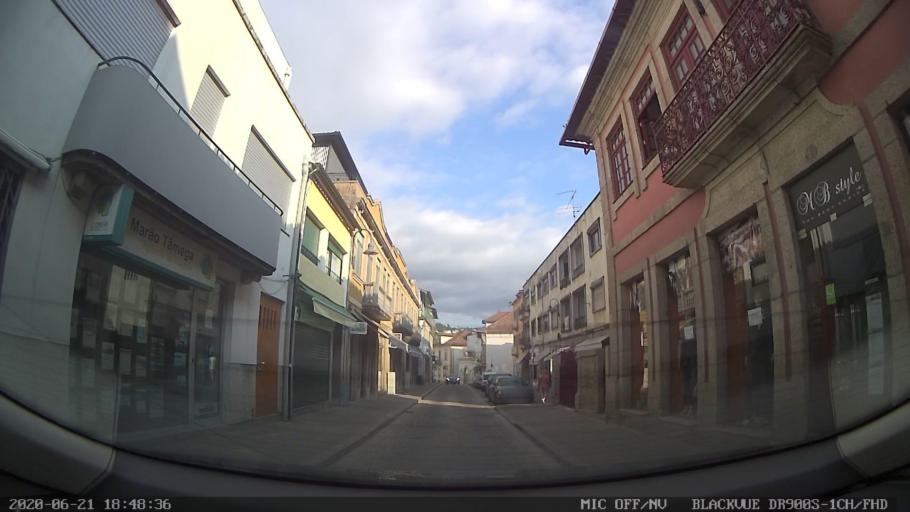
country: PT
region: Porto
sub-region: Amarante
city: Amarante
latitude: 41.2703
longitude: -8.0823
